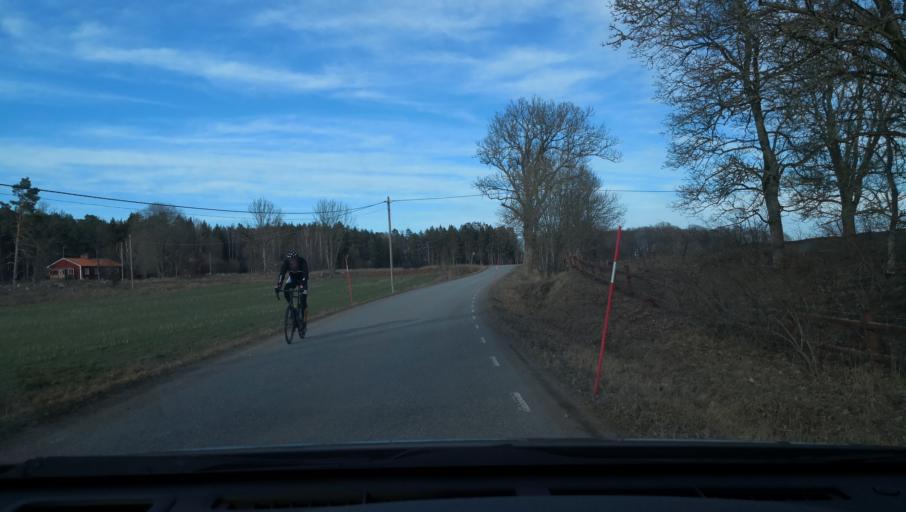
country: SE
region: Uppsala
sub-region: Enkopings Kommun
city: Grillby
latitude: 59.5447
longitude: 17.2061
